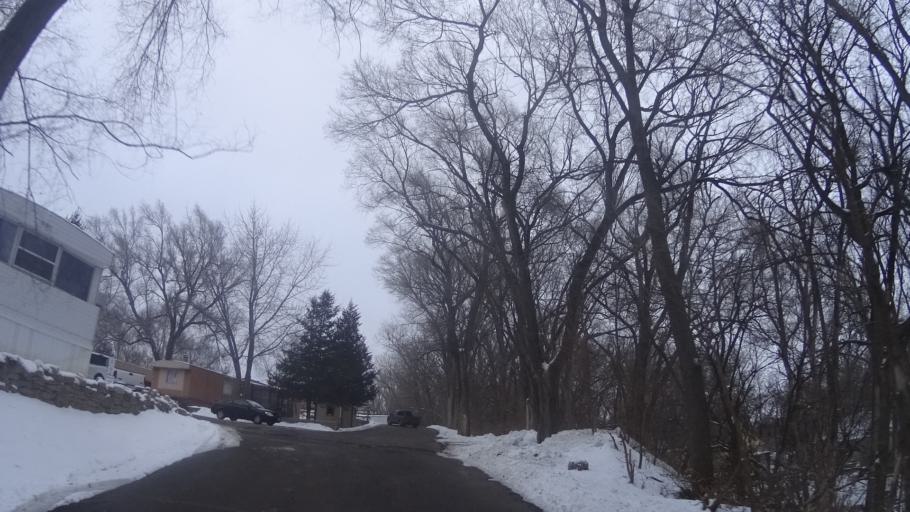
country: US
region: Nebraska
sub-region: Sarpy County
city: Offutt Air Force Base
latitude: 41.1376
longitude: -95.9240
